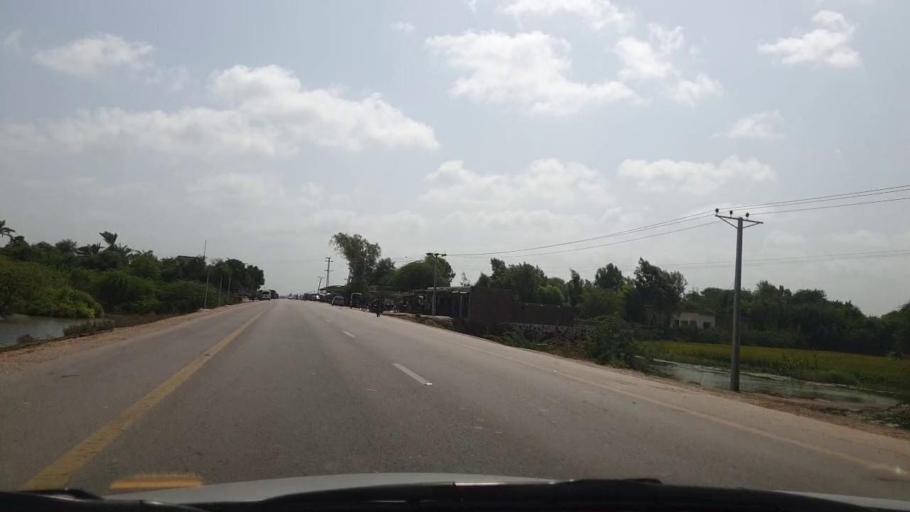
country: PK
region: Sindh
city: Talhar
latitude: 24.9089
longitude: 68.7360
